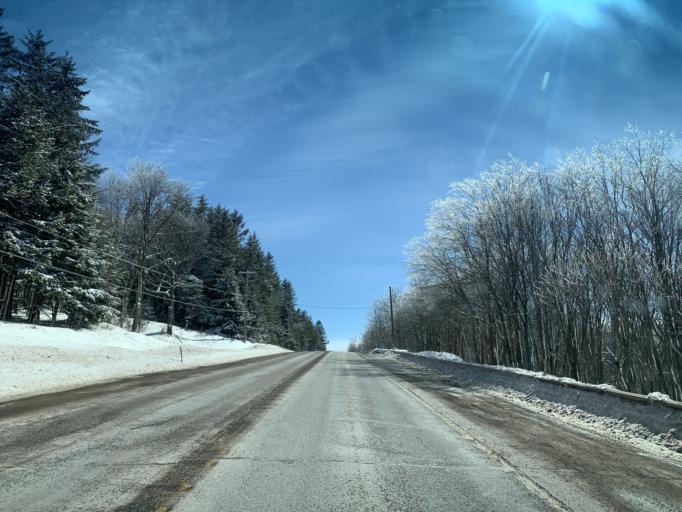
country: US
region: Pennsylvania
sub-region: Somerset County
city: Meyersdale
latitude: 39.7000
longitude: -79.2566
